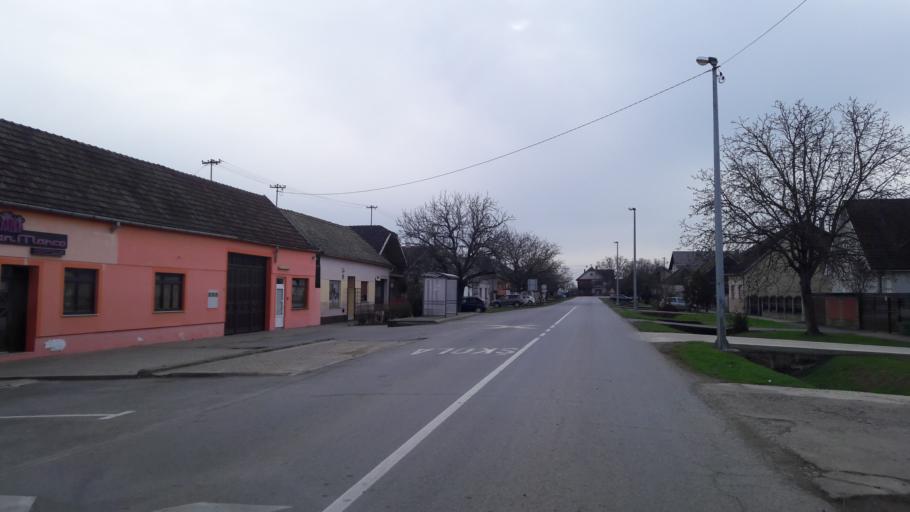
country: HR
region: Osjecko-Baranjska
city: Semeljci
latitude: 45.3841
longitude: 18.5625
